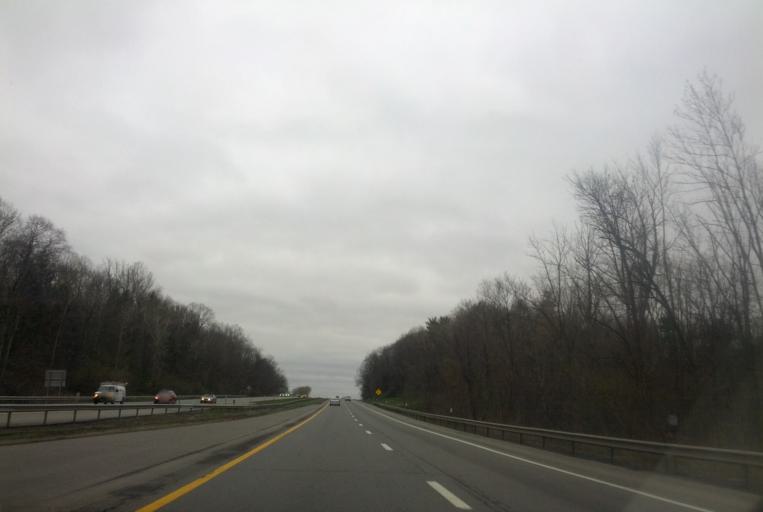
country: US
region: New York
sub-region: Ontario County
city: Phelps
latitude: 42.9551
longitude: -76.9910
